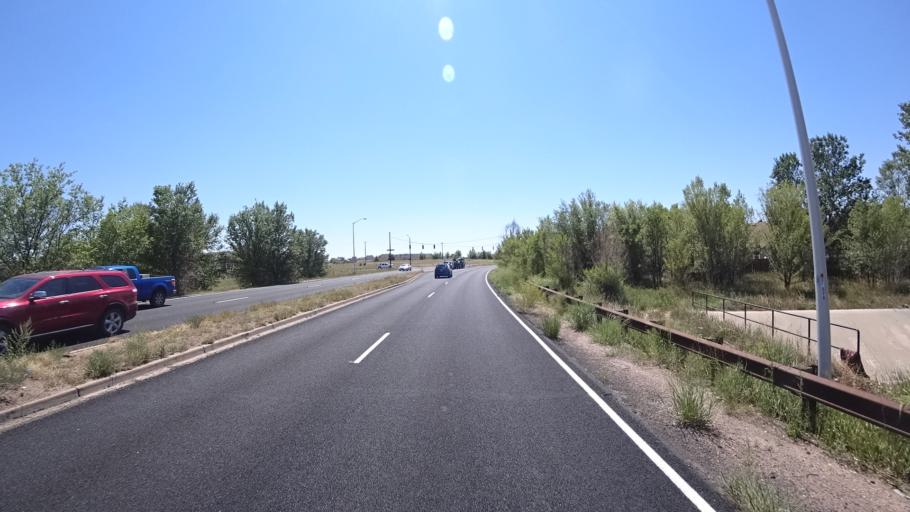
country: US
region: Colorado
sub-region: El Paso County
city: Stratmoor
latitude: 38.7872
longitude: -104.7408
